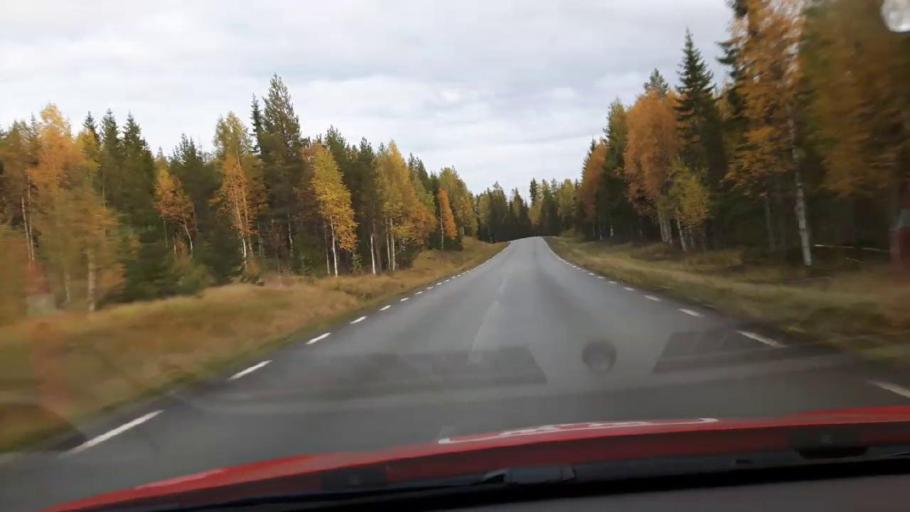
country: SE
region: Jaemtland
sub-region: OEstersunds Kommun
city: Lit
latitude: 63.3141
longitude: 15.0982
